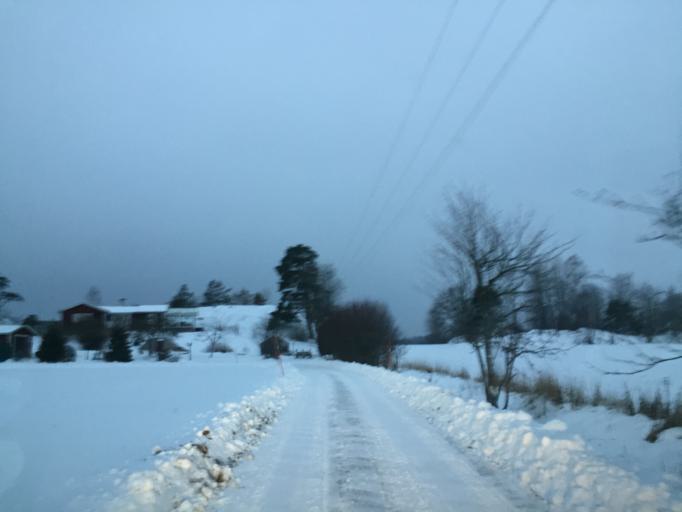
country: SE
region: Stockholm
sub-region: Sodertalje Kommun
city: Pershagen
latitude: 59.0742
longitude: 17.5870
